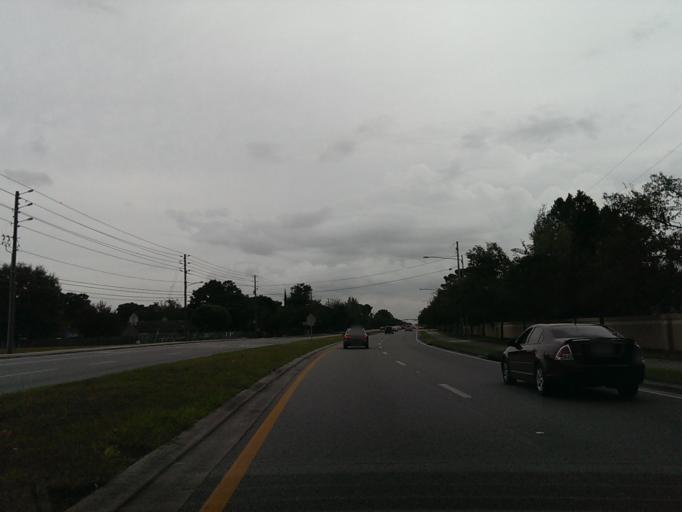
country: US
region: Florida
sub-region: Orange County
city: Gotha
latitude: 28.5411
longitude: -81.4938
